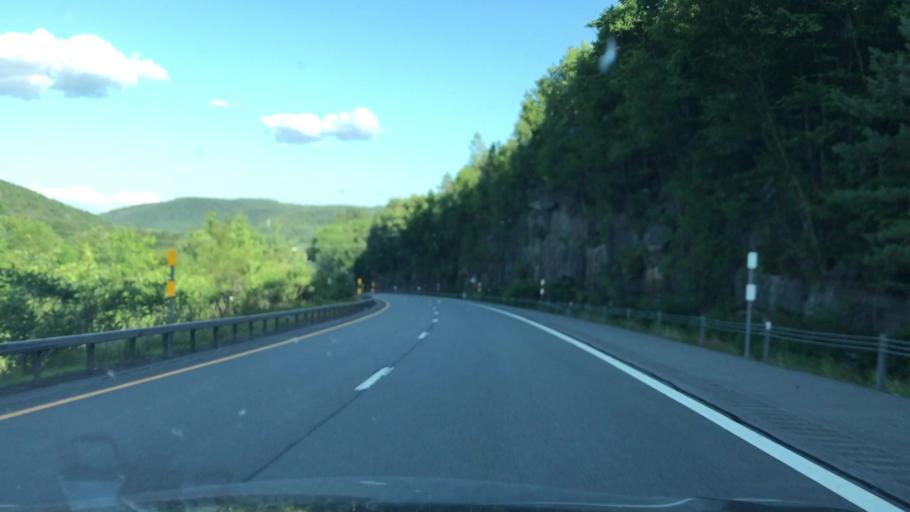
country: US
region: New York
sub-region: Sullivan County
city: Livingston Manor
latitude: 41.9372
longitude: -74.9269
